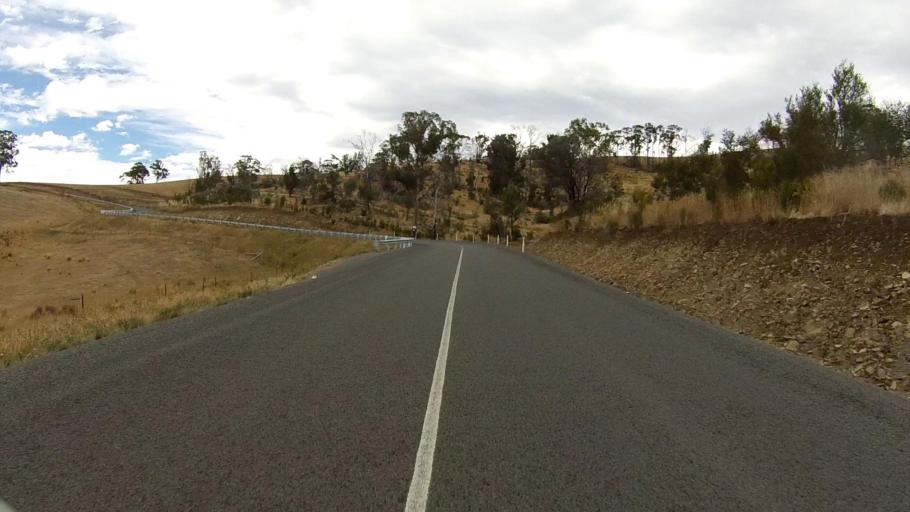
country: AU
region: Tasmania
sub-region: Sorell
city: Sorell
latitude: -42.8829
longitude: 147.7185
